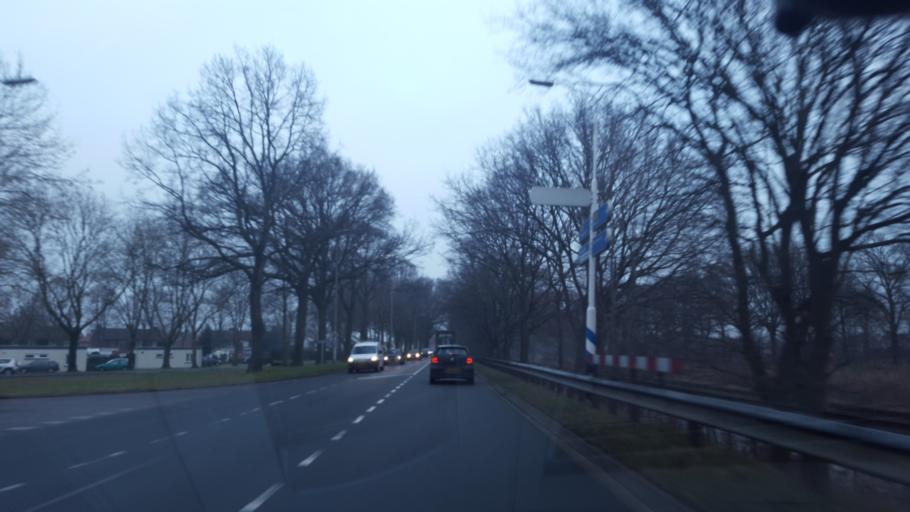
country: NL
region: Limburg
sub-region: Gemeente Nederweert
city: Nederweert
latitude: 51.2866
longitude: 5.7538
